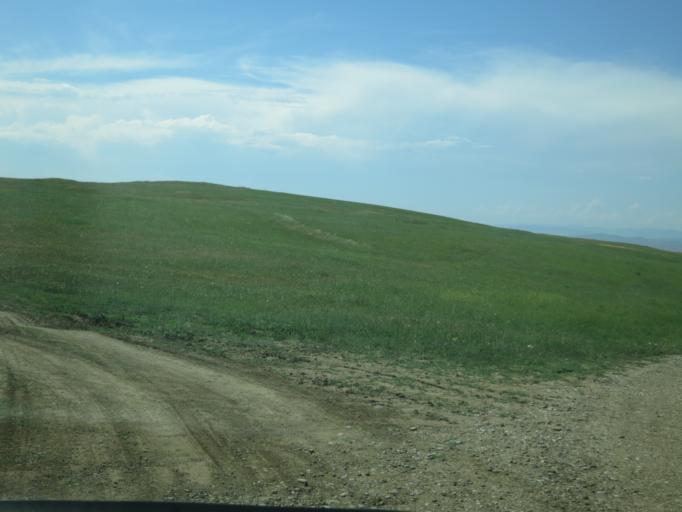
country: GE
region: Kvemo Kartli
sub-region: Gardabani
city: Gardabani
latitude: 41.4740
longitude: 45.2946
